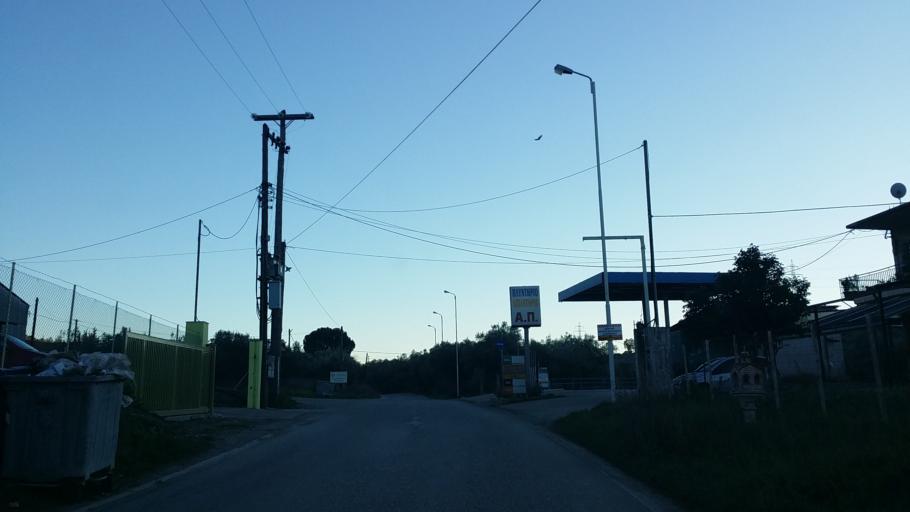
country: GR
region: West Greece
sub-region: Nomos Aitolias kai Akarnanias
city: Neapolis
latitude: 38.6988
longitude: 21.3531
